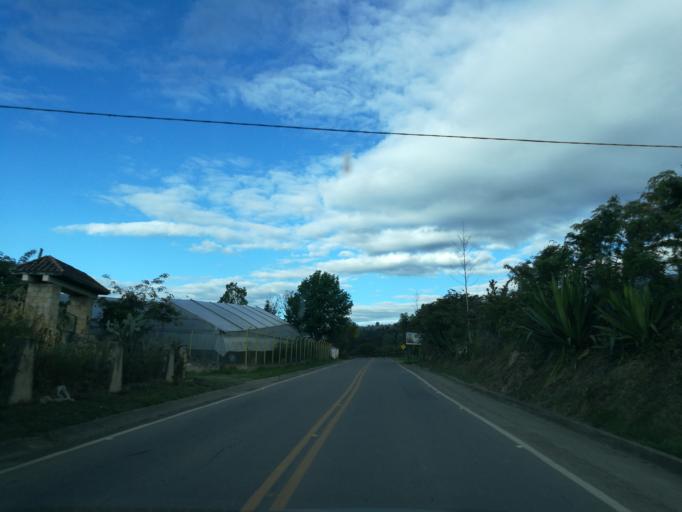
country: CO
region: Boyaca
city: Sutamarchan
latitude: 5.6120
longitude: -73.6276
